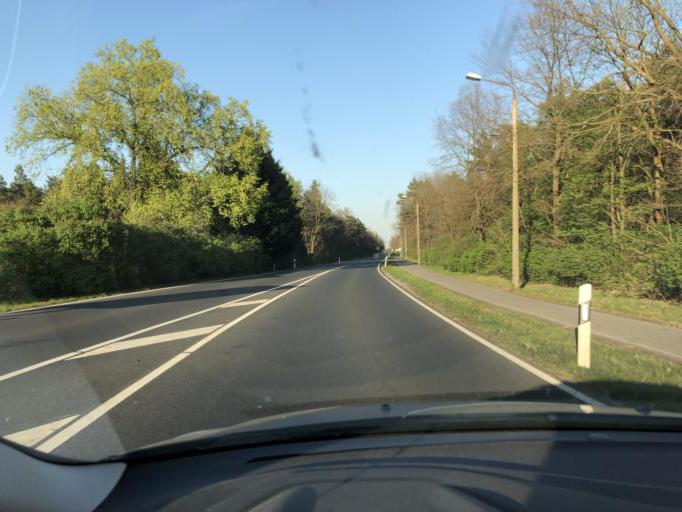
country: DE
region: Brandenburg
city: Ruhland
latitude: 51.4766
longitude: 13.9015
